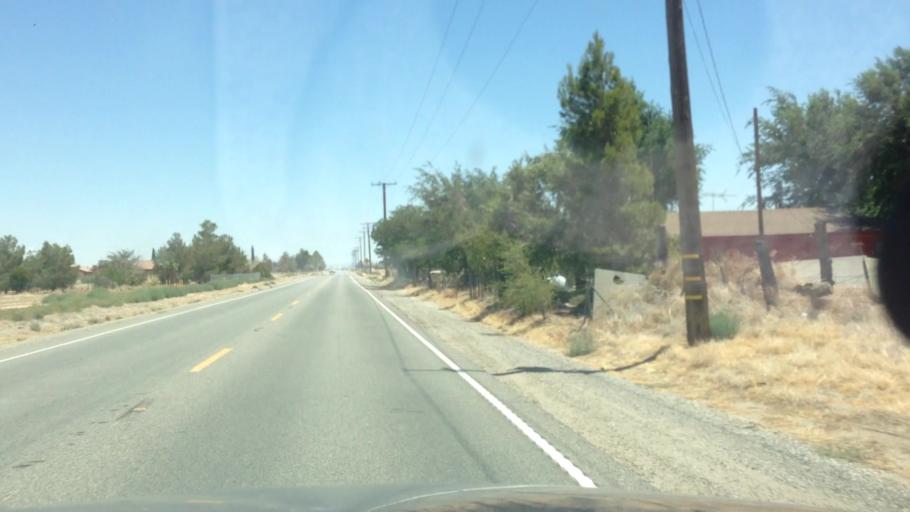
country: US
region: California
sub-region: Los Angeles County
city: Quartz Hill
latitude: 34.7764
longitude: -118.2849
